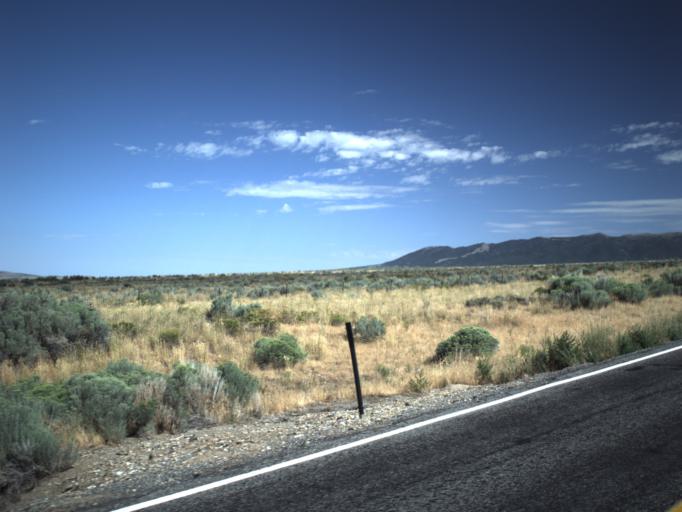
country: US
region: Utah
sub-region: Juab County
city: Mona
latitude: 39.8876
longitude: -112.1380
